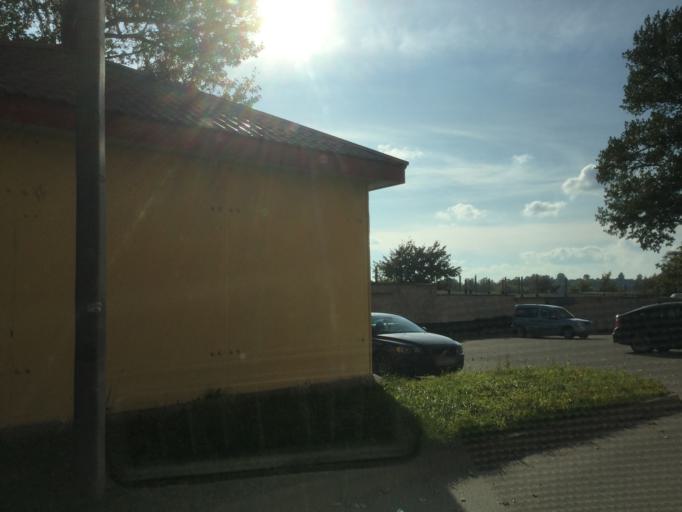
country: BY
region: Vitebsk
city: Vitebsk
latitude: 55.1717
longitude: 30.1939
